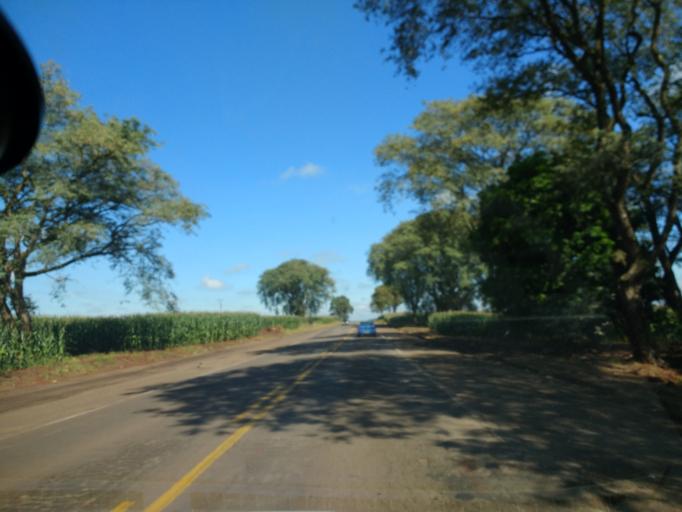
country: BR
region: Parana
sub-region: Terra Boa
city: Terra Boa
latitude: -23.6087
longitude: -52.4195
